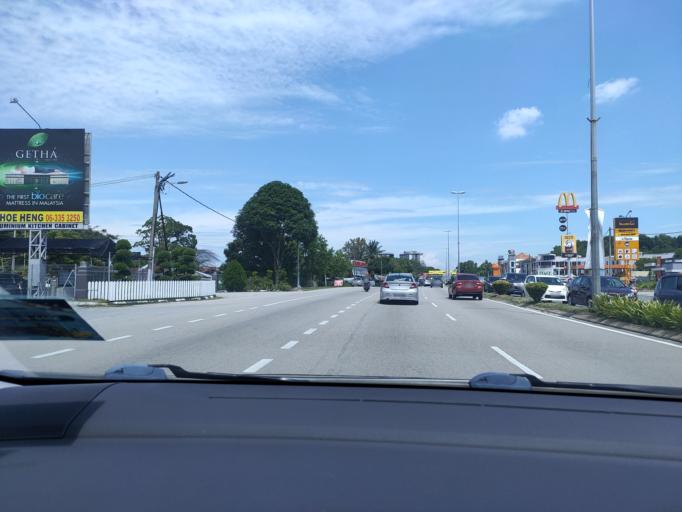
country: MY
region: Melaka
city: Batu Berendam
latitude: 2.2550
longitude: 102.2226
